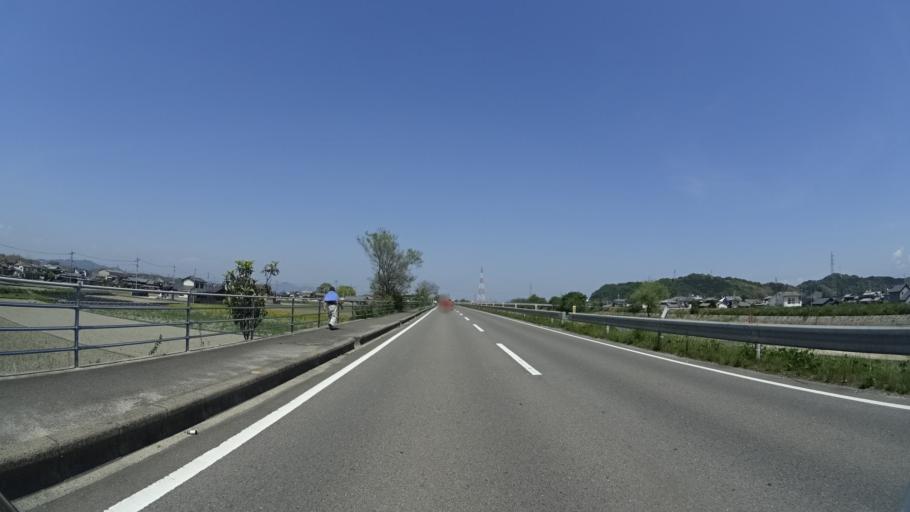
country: JP
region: Ehime
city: Hojo
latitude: 34.0310
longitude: 132.9662
